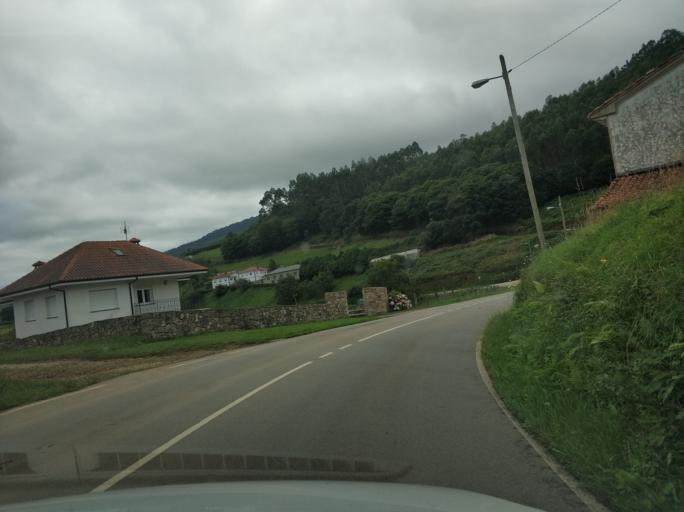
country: ES
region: Asturias
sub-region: Province of Asturias
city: Cudillero
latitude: 43.5411
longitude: -6.2292
